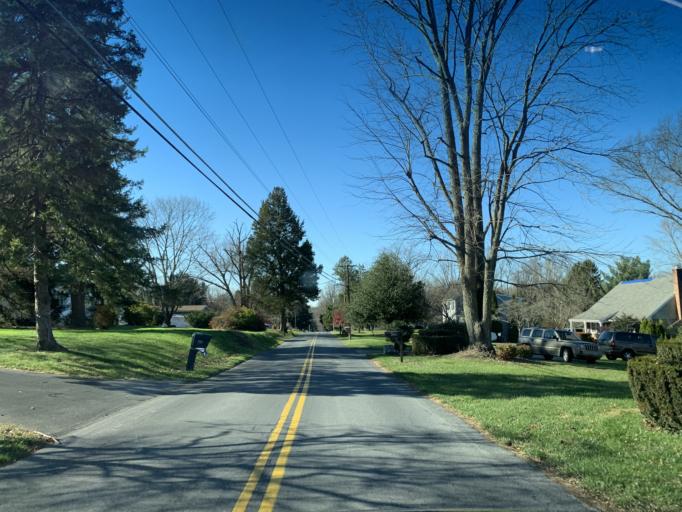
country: US
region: Maryland
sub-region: Harford County
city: Bel Air South
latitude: 39.4992
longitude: -76.3387
